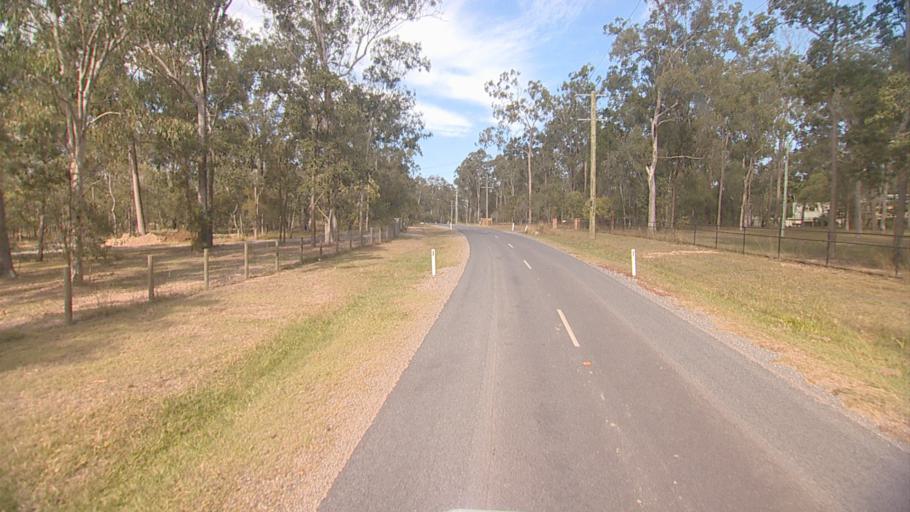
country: AU
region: Queensland
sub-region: Logan
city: North Maclean
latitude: -27.7524
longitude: 152.9736
